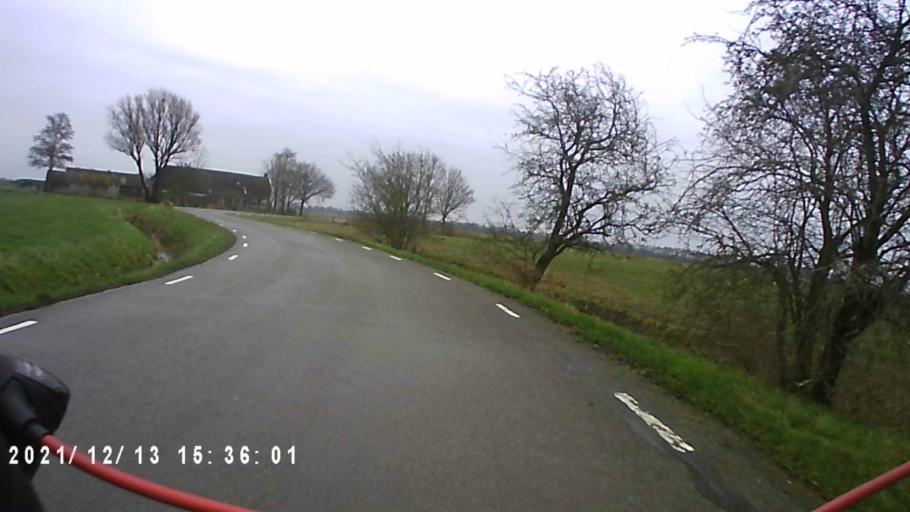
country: NL
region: Groningen
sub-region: Gemeente Appingedam
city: Appingedam
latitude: 53.3301
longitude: 6.8280
